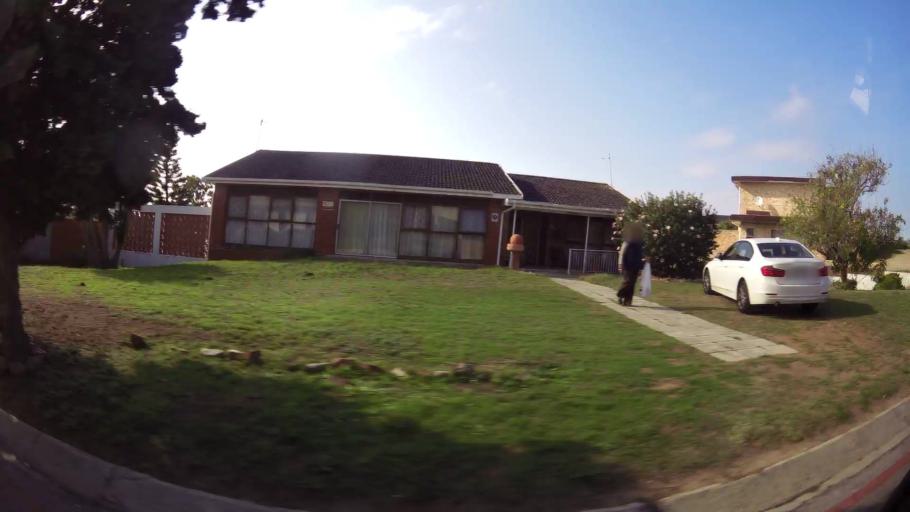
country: ZA
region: Eastern Cape
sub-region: Nelson Mandela Bay Metropolitan Municipality
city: Port Elizabeth
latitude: -33.9306
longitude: 25.5486
